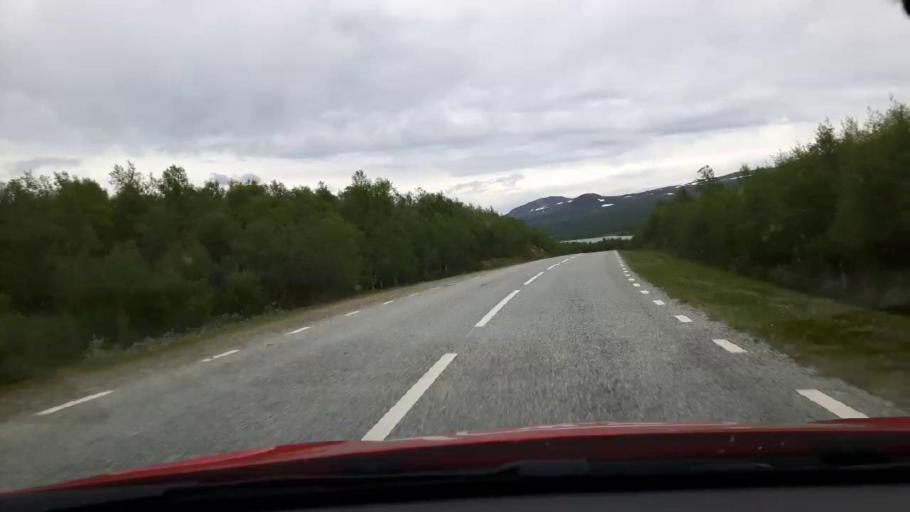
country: NO
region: Sor-Trondelag
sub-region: Tydal
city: Aas
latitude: 62.6202
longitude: 12.1338
